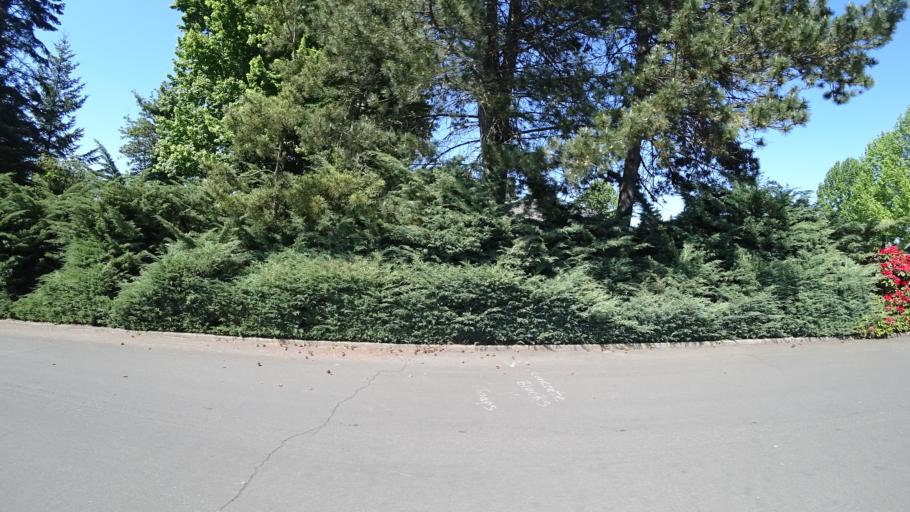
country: US
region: Oregon
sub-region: Washington County
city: Rockcreek
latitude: 45.5492
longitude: -122.8806
